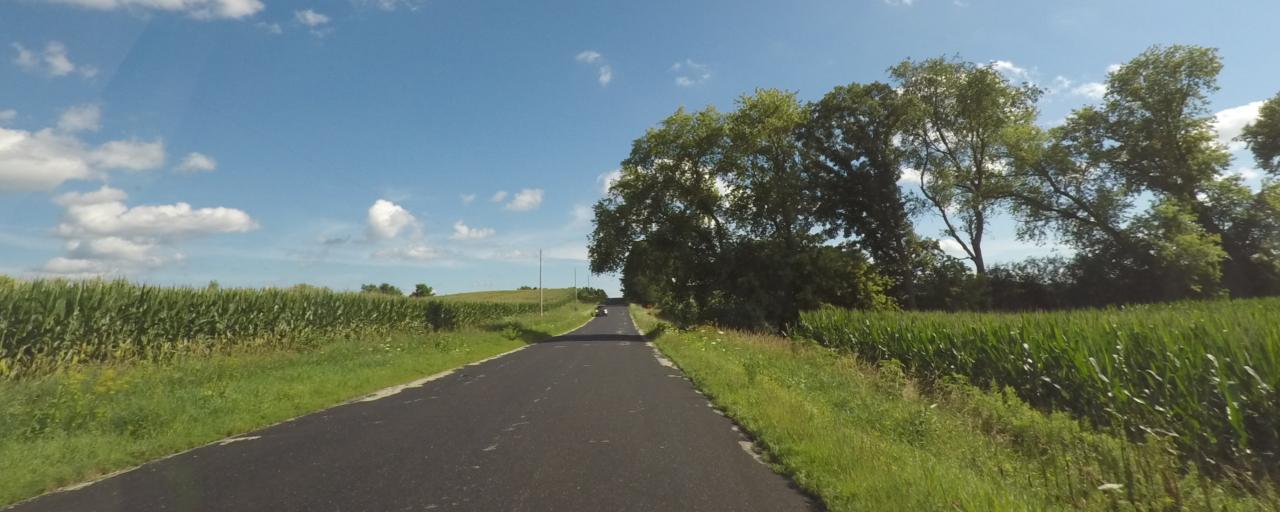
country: US
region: Wisconsin
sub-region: Rock County
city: Edgerton
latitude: 42.8657
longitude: -89.1320
